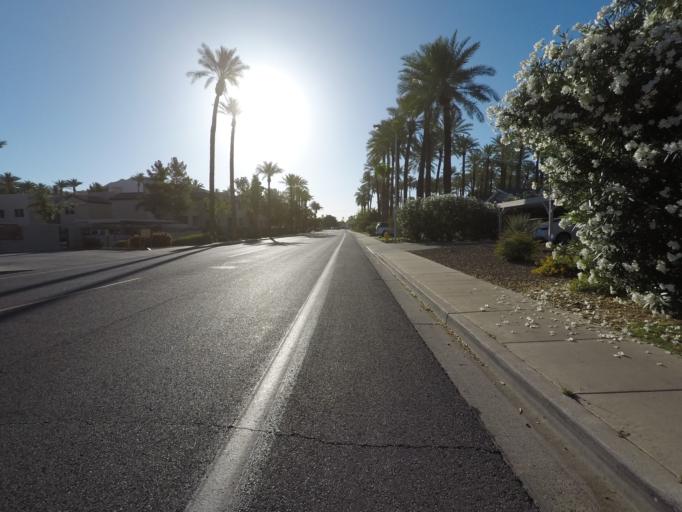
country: US
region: Arizona
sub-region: Maricopa County
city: Paradise Valley
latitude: 33.5022
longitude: -111.9892
